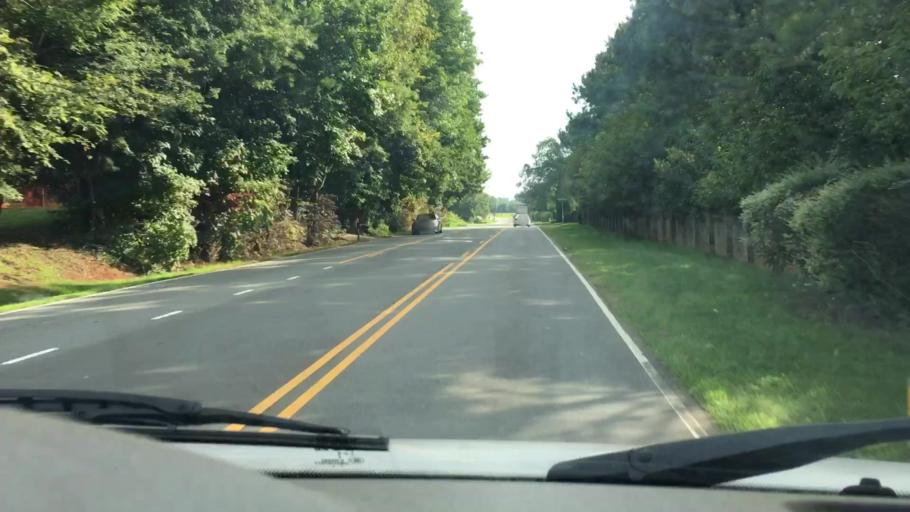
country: US
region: North Carolina
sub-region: Mecklenburg County
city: Huntersville
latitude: 35.3724
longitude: -80.8067
